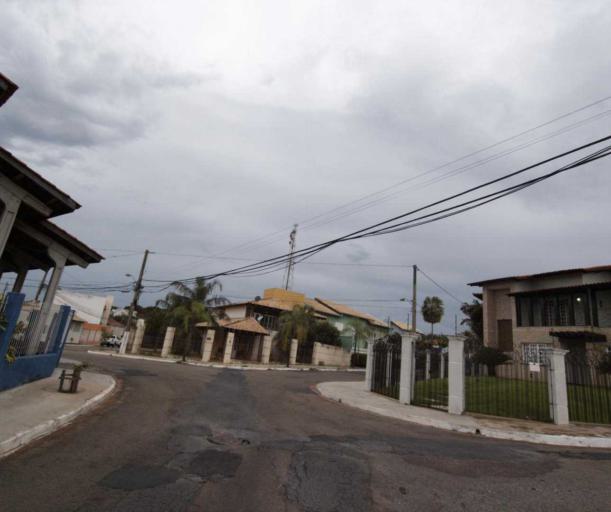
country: BR
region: Mato Grosso
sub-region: Cuiaba
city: Cuiaba
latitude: -15.6031
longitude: -56.0810
